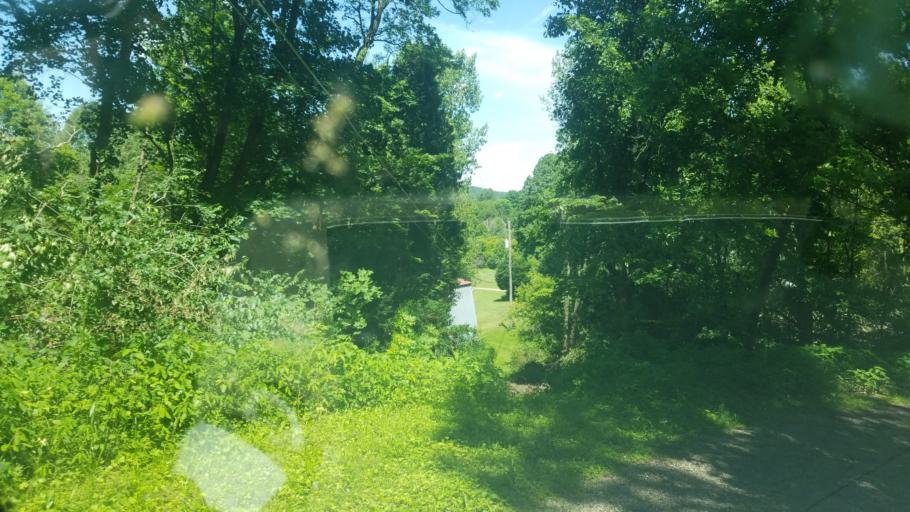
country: US
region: Ohio
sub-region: Sandusky County
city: Bellville
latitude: 40.6312
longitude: -82.5334
